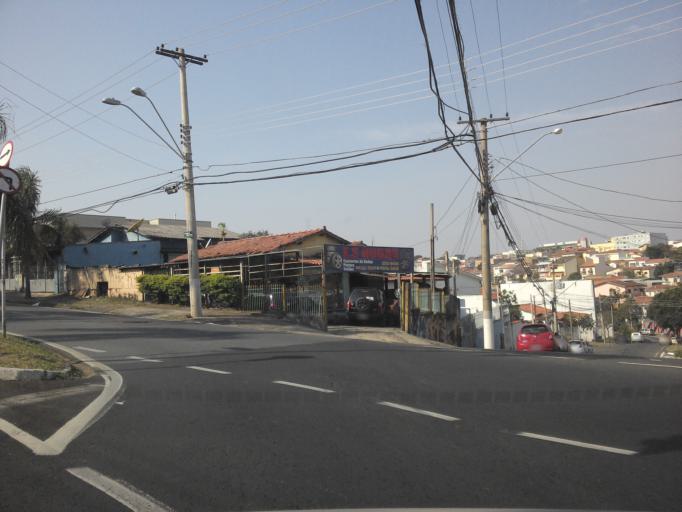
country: BR
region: Sao Paulo
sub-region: Campinas
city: Campinas
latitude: -22.9078
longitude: -47.0843
